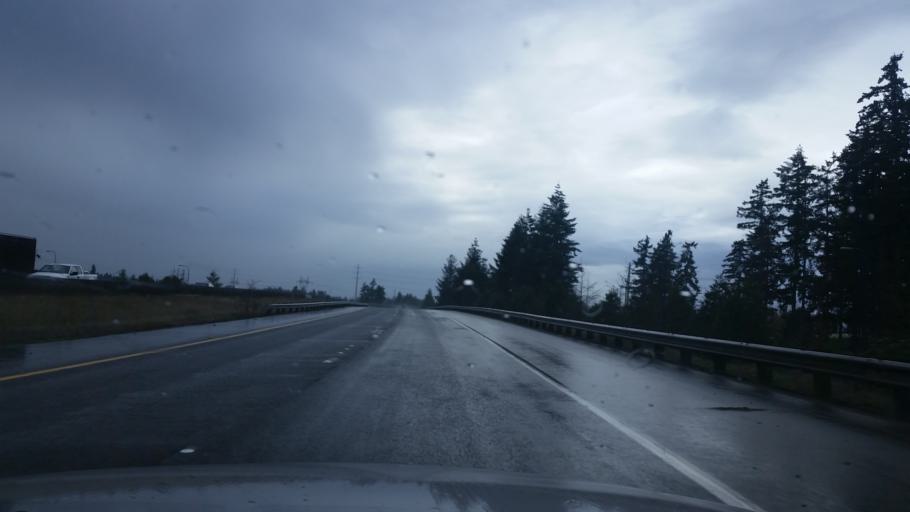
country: US
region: Washington
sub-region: King County
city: Covington
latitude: 47.3596
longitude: -122.1194
